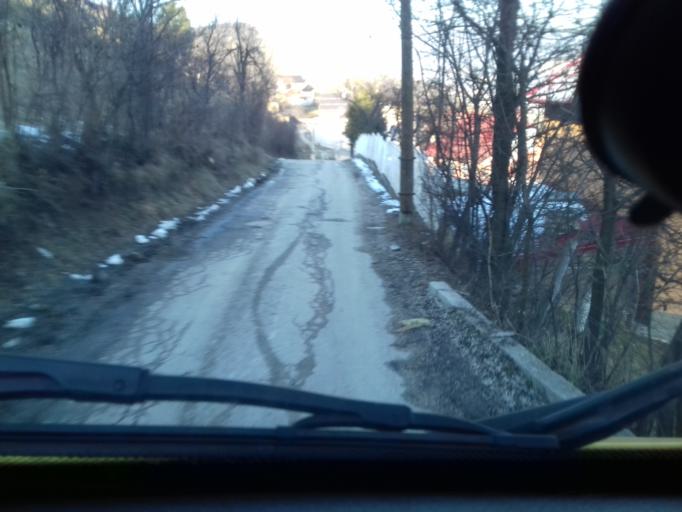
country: BA
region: Federation of Bosnia and Herzegovina
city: Zenica
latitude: 44.1875
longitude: 17.9009
